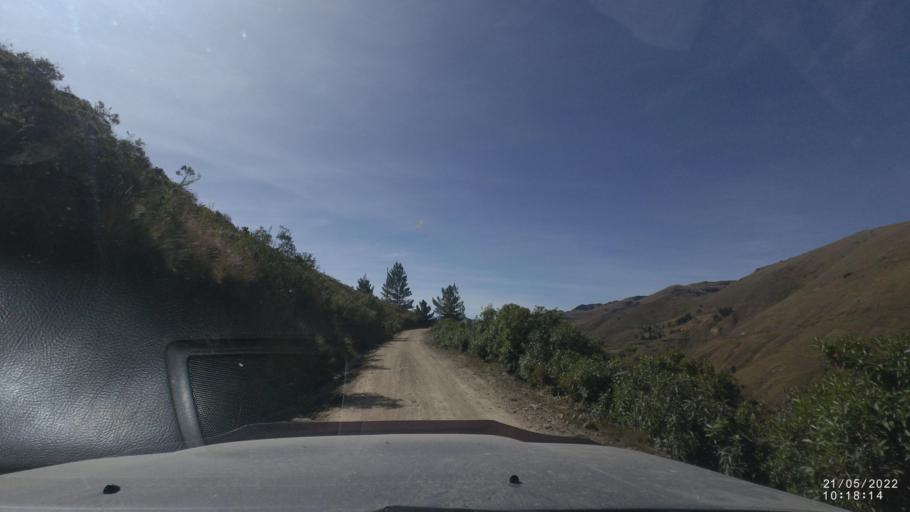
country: BO
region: Cochabamba
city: Colomi
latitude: -17.3275
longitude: -65.9621
